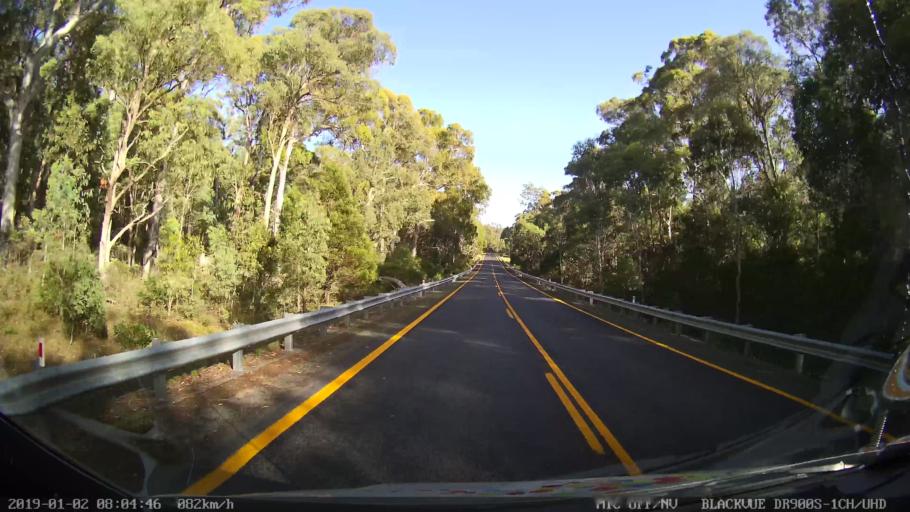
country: AU
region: New South Wales
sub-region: Tumut Shire
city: Tumut
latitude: -35.6589
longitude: 148.3917
